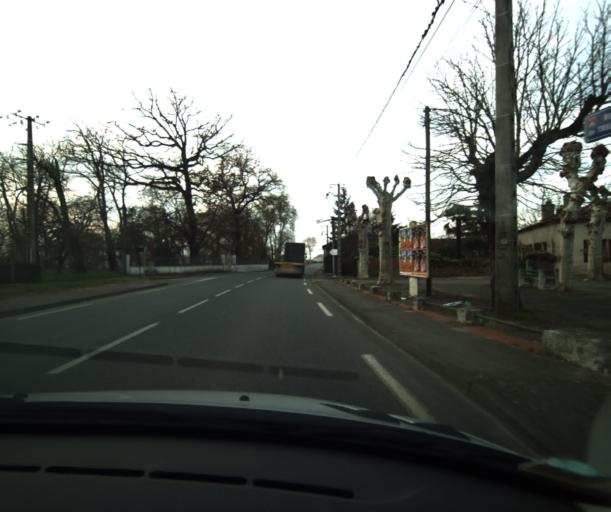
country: FR
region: Midi-Pyrenees
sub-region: Departement du Tarn-et-Garonne
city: Saint-Porquier
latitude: 44.0203
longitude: 1.1579
